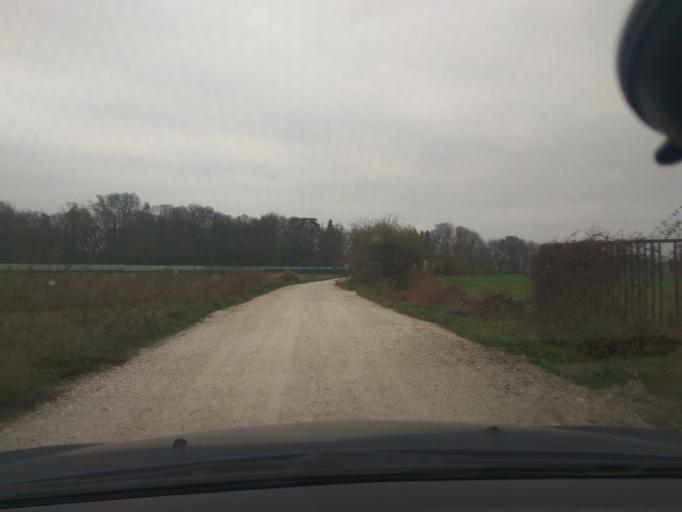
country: SK
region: Trnavsky
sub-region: Okres Trnava
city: Piestany
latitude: 48.6070
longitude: 17.8605
